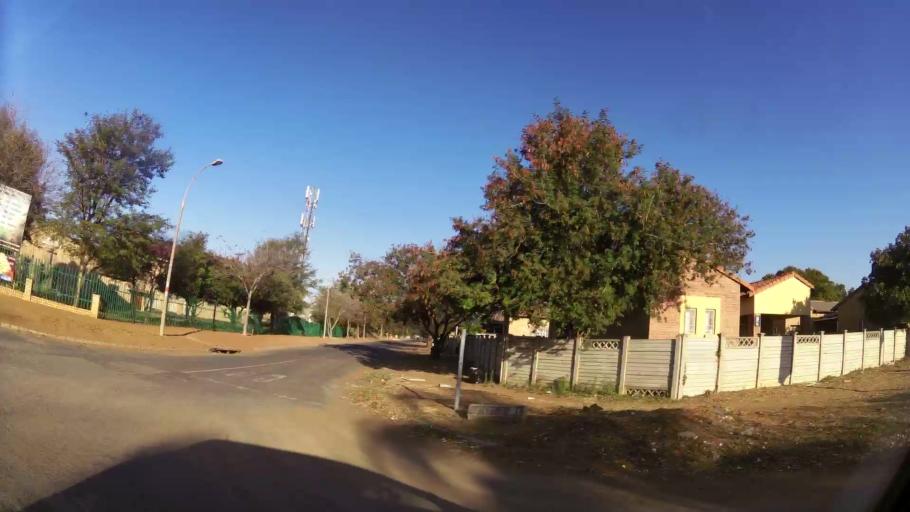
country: ZA
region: North-West
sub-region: Bojanala Platinum District Municipality
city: Rustenburg
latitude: -25.6799
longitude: 27.2169
